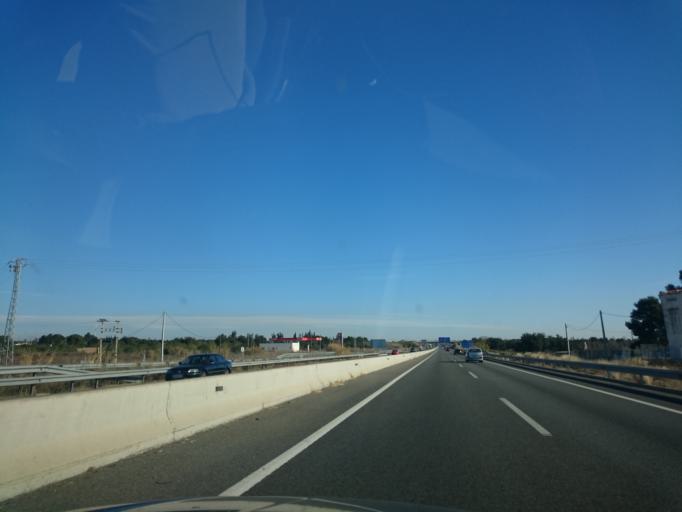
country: ES
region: Catalonia
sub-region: Provincia de Tarragona
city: Salou
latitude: 41.0965
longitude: 1.1116
